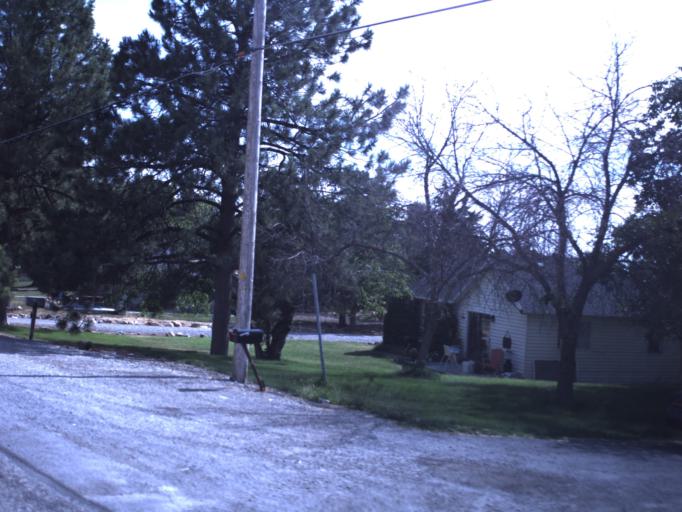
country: US
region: Utah
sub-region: Box Elder County
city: Honeyville
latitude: 41.6614
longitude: -112.0877
